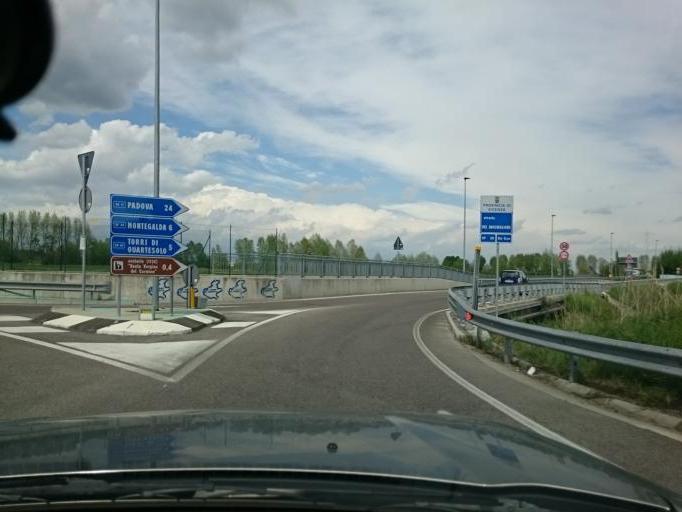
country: IT
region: Veneto
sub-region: Provincia di Vicenza
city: Longare
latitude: 45.4798
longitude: 11.6105
